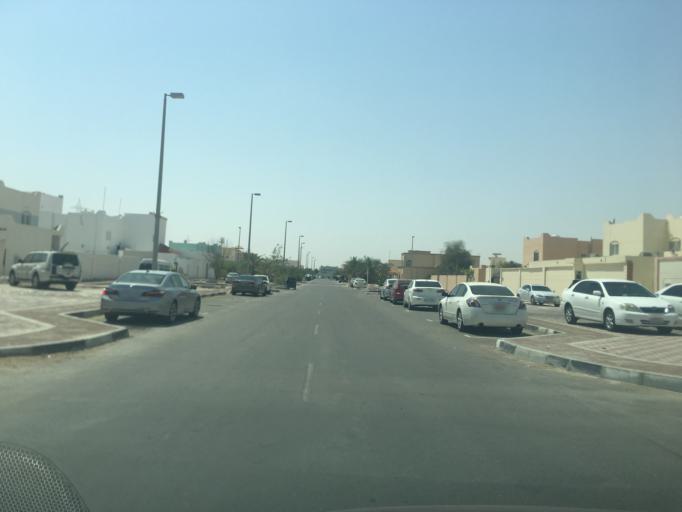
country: AE
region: Abu Dhabi
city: Abu Dhabi
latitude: 24.3121
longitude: 54.6372
